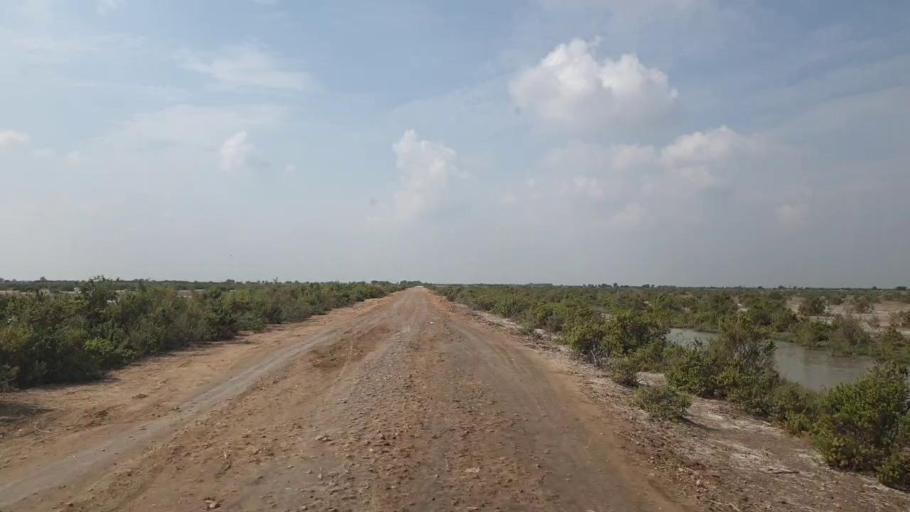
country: PK
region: Sindh
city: Badin
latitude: 24.5066
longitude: 68.6135
